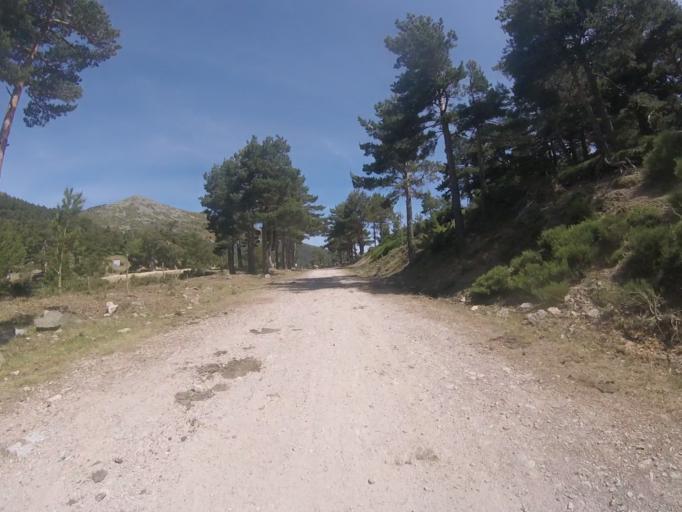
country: ES
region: Madrid
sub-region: Provincia de Madrid
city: Cercedilla
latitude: 40.7916
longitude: -4.0595
